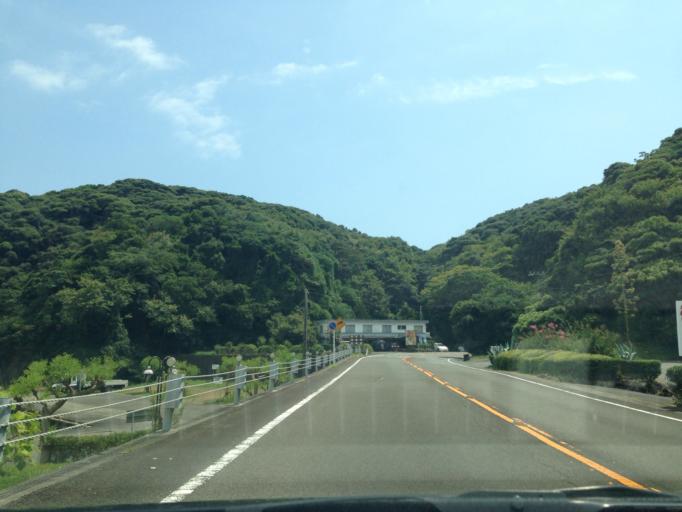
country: JP
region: Shizuoka
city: Shimoda
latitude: 34.6289
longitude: 138.8881
